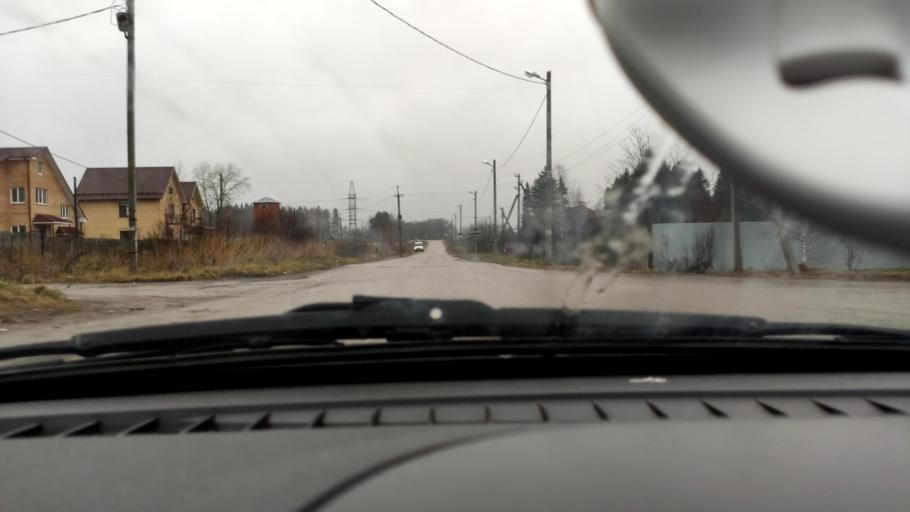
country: RU
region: Perm
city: Perm
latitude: 58.0390
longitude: 56.4082
